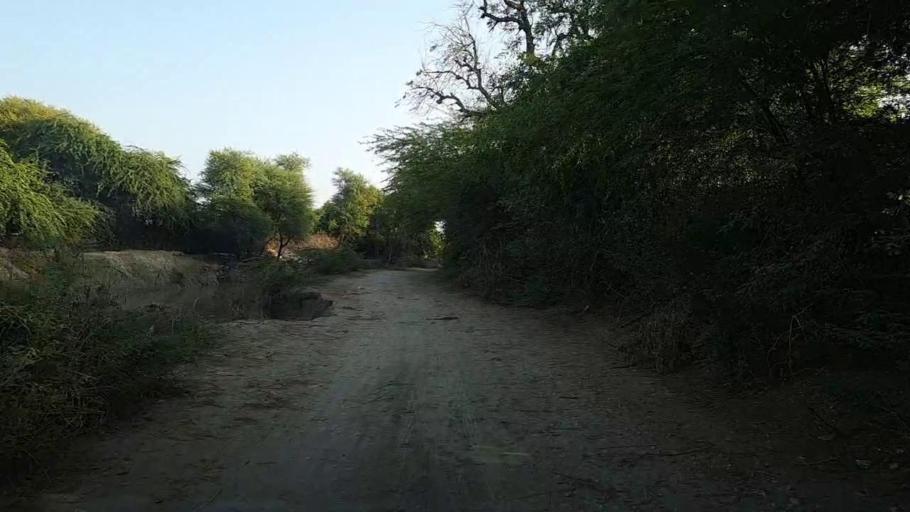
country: PK
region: Sindh
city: Kario
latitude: 24.6965
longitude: 68.6712
